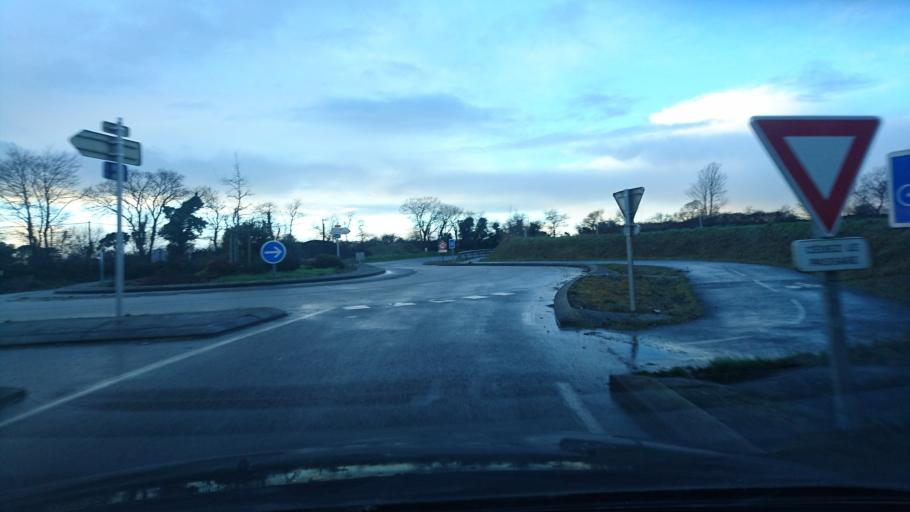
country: FR
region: Brittany
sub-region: Departement du Finistere
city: Guilers
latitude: 48.4117
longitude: -4.5601
